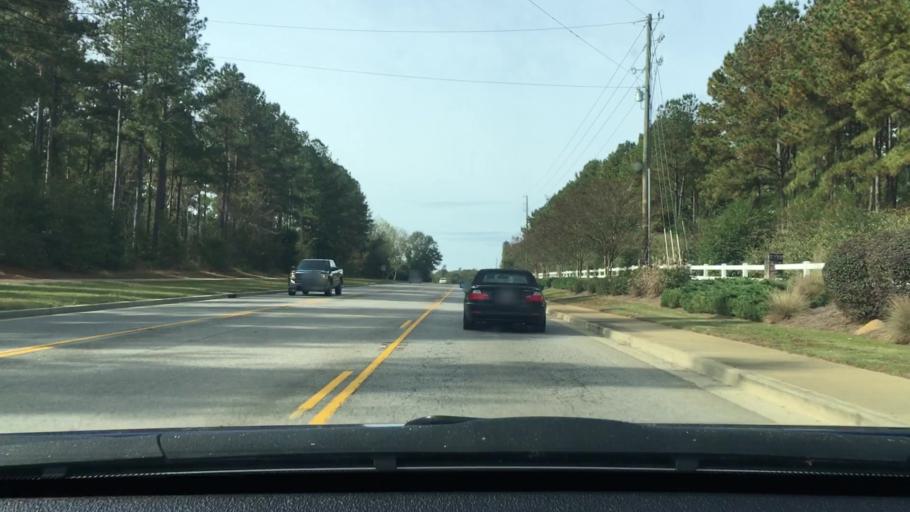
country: US
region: South Carolina
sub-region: Sumter County
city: South Sumter
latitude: 33.9198
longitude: -80.3939
